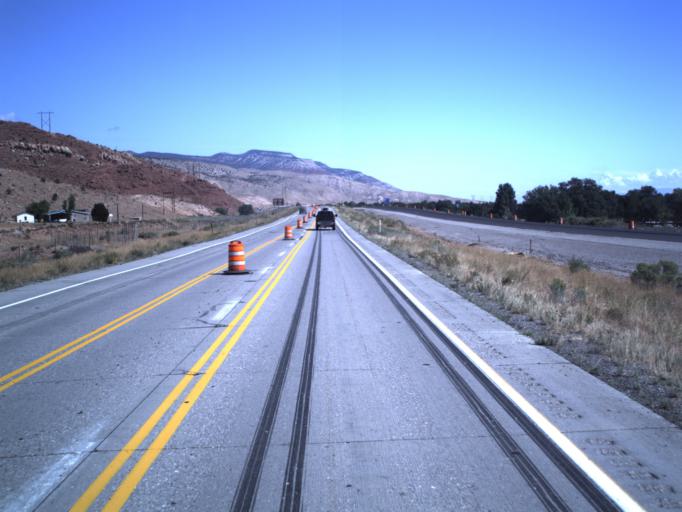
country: US
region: Utah
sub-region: Sevier County
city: Richfield
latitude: 38.7668
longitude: -112.1023
